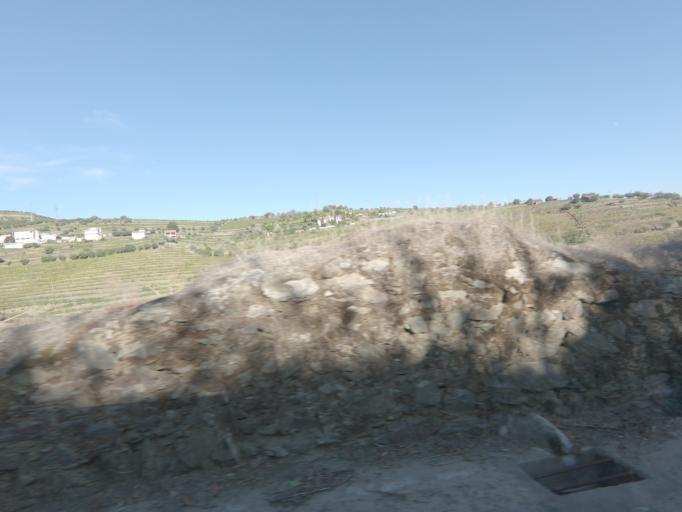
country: PT
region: Vila Real
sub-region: Peso da Regua
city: Peso da Regua
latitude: 41.1767
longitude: -7.7810
